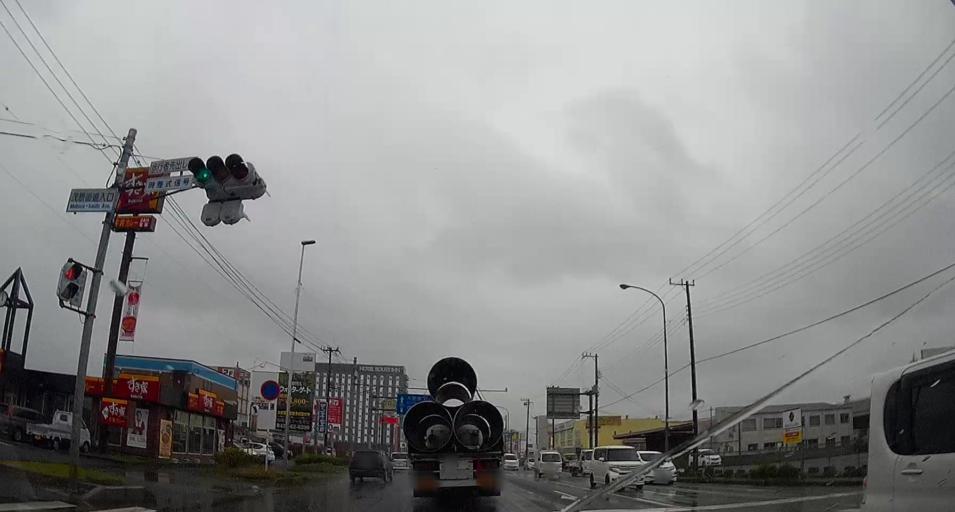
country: JP
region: Chiba
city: Chiba
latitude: 35.5555
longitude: 140.1257
